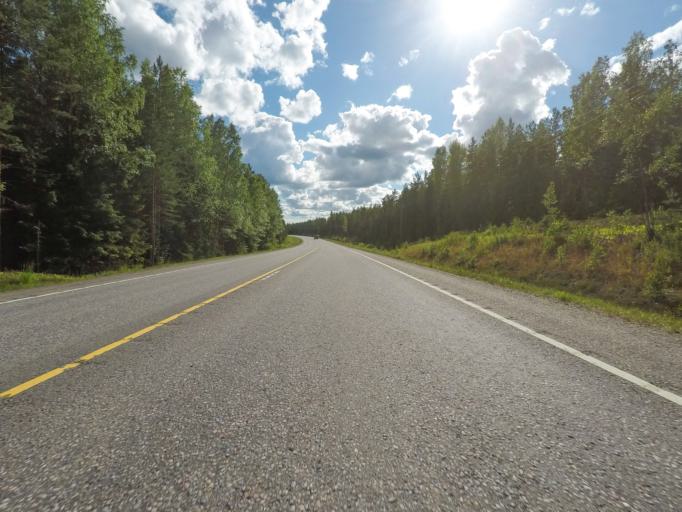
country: FI
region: Uusimaa
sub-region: Helsinki
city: Nurmijaervi
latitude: 60.5326
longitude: 24.6813
